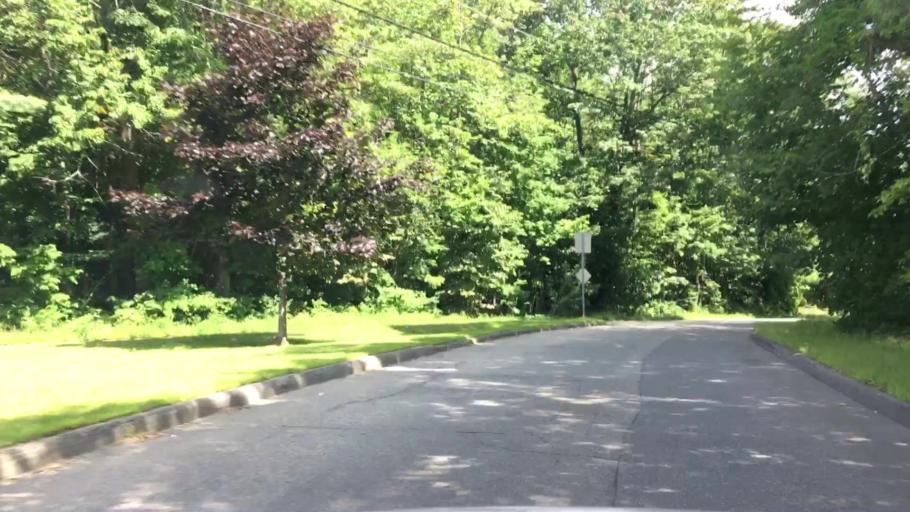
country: US
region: Maine
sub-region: Kennebec County
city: Augusta
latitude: 44.3193
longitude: -69.8176
